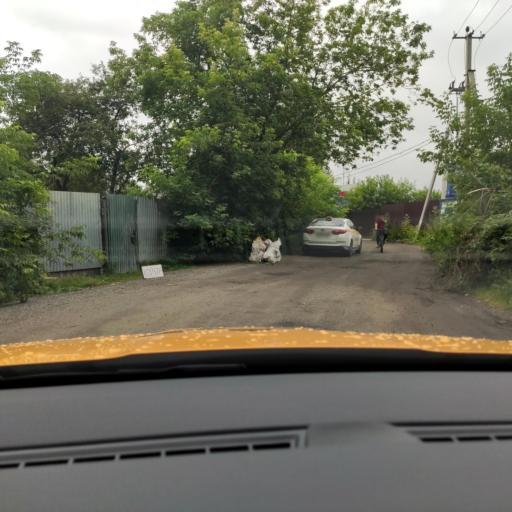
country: RU
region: Moscow
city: Vostochnyy
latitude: 55.8172
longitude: 37.8434
